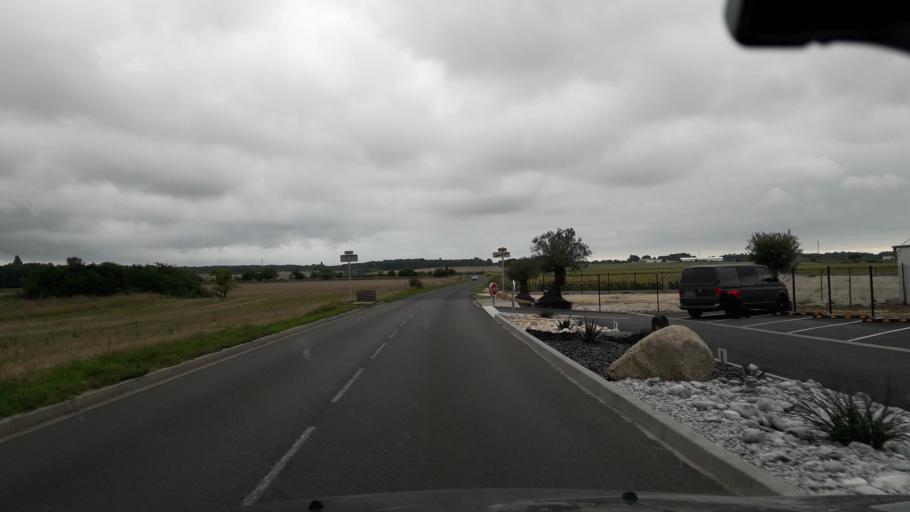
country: FR
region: Poitou-Charentes
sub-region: Departement de la Charente-Maritime
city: Arvert
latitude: 45.7362
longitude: -1.1290
